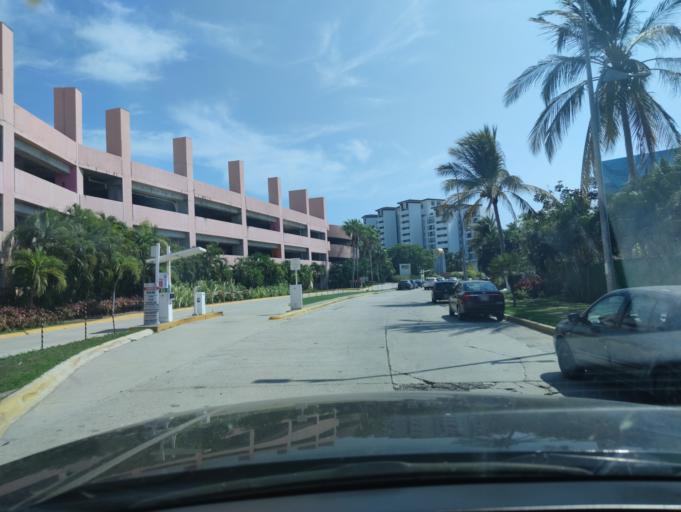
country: MX
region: Guerrero
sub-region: Acapulco de Juarez
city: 10 de Abril
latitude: 16.7725
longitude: -99.7773
